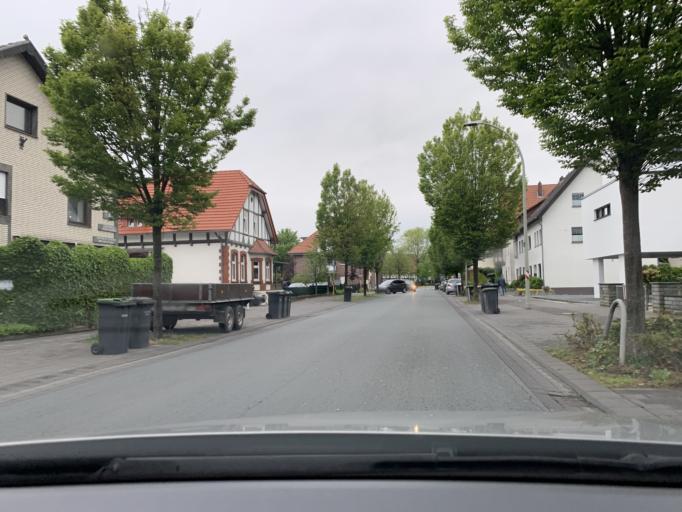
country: DE
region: North Rhine-Westphalia
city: Rietberg
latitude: 51.8051
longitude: 8.4242
